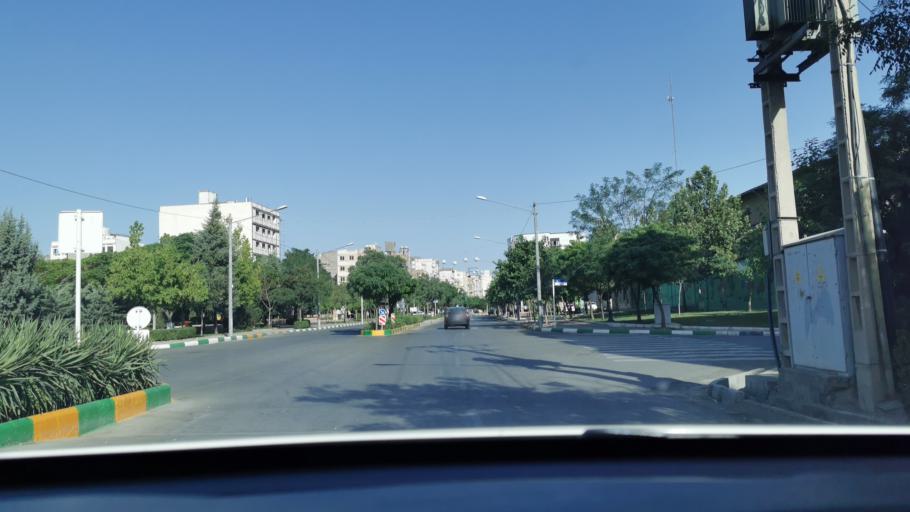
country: IR
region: Razavi Khorasan
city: Mashhad
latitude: 36.3382
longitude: 59.5091
